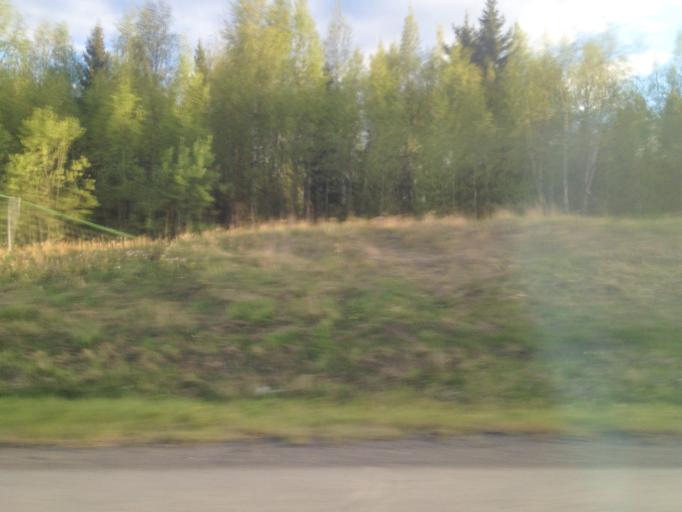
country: FI
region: Pirkanmaa
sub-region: Etelae-Pirkanmaa
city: Akaa
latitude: 61.1880
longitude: 23.8758
